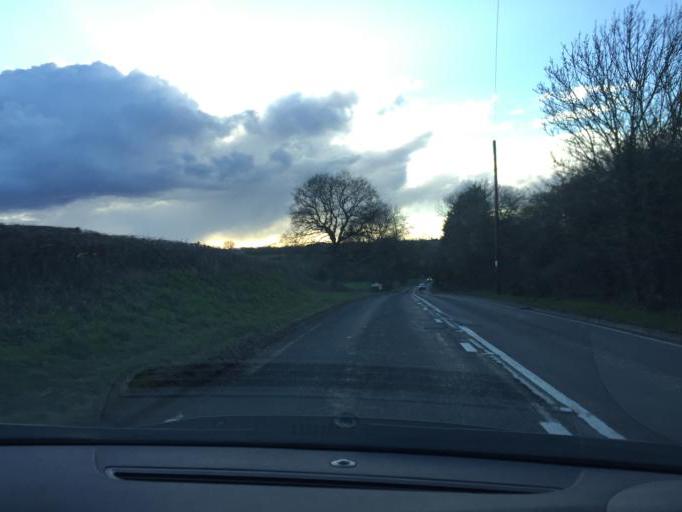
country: GB
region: England
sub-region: Warwickshire
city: Wroxall
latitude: 52.2737
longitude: -1.6813
